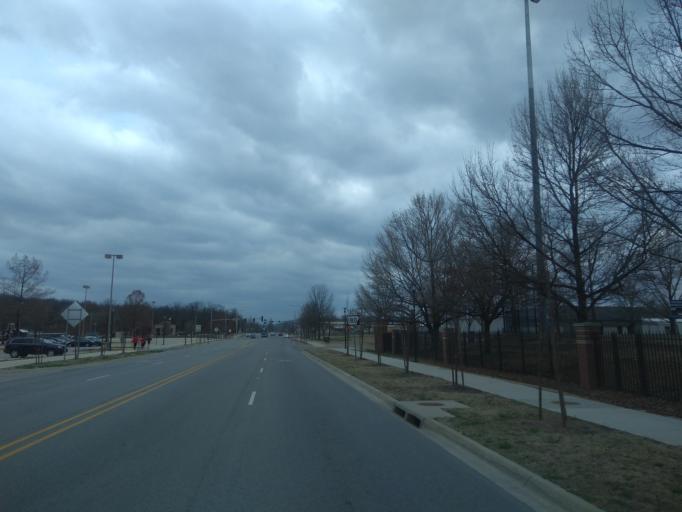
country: US
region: Arkansas
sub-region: Washington County
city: Fayetteville
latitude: 36.0587
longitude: -94.1804
